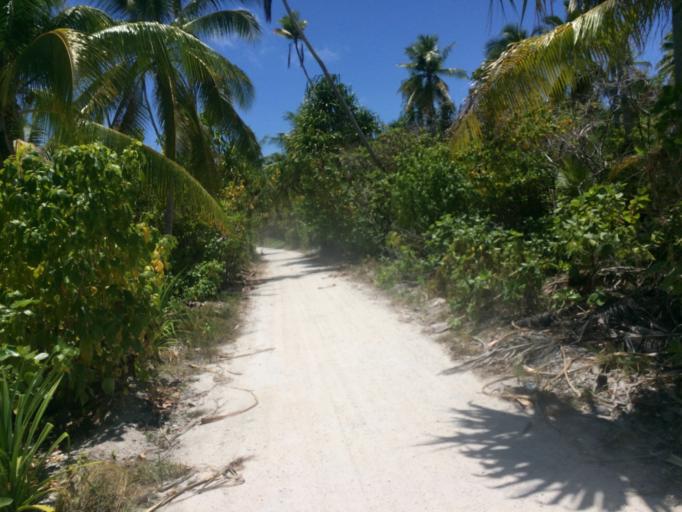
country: KI
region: Gilbert Islands
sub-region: Marakei
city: Rawannawi Village
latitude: 1.7739
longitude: 173.0456
